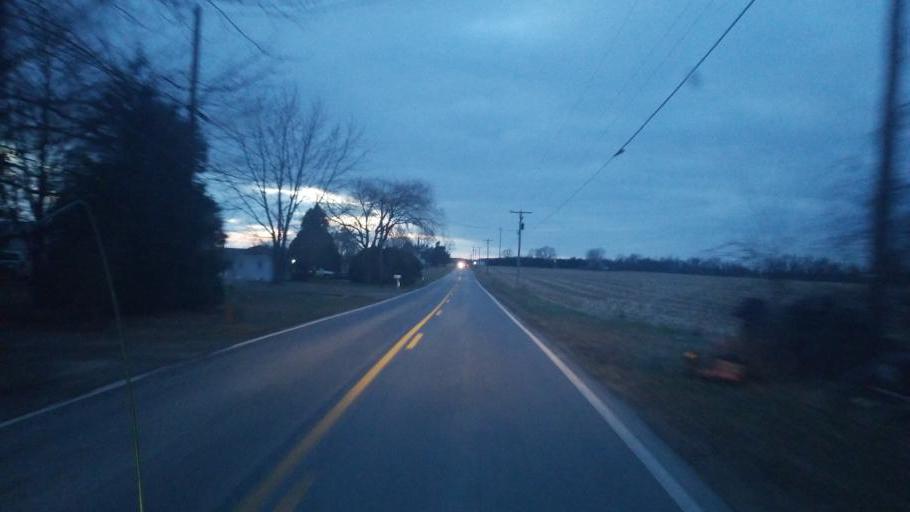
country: US
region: Ohio
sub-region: Marion County
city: Prospect
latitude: 40.4341
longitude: -83.0754
